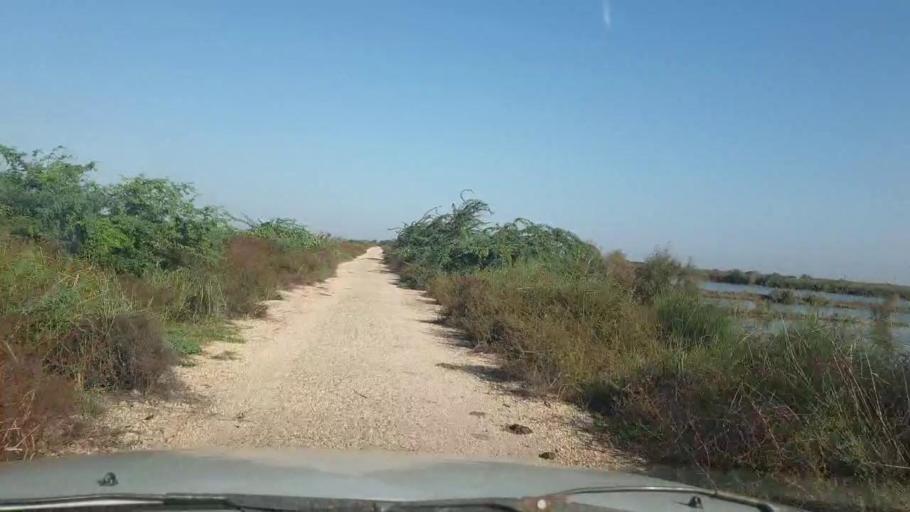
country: PK
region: Sindh
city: Chuhar Jamali
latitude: 24.5515
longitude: 67.9093
